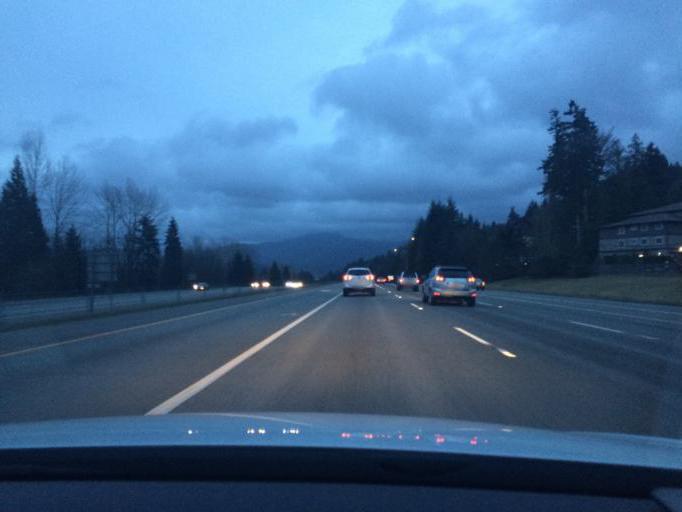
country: US
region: Washington
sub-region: King County
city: West Lake Sammamish
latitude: 47.5615
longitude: -122.0929
